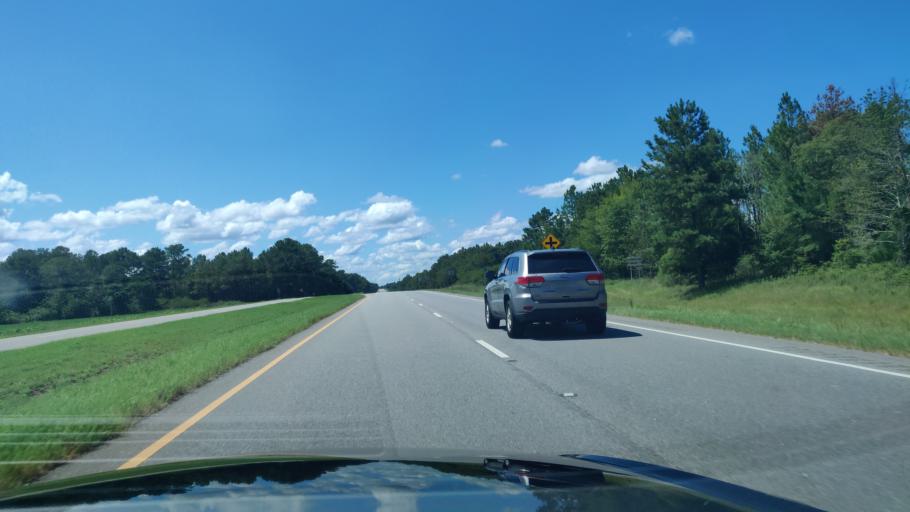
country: US
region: Georgia
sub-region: Terrell County
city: Dawson
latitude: 31.8762
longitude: -84.4973
